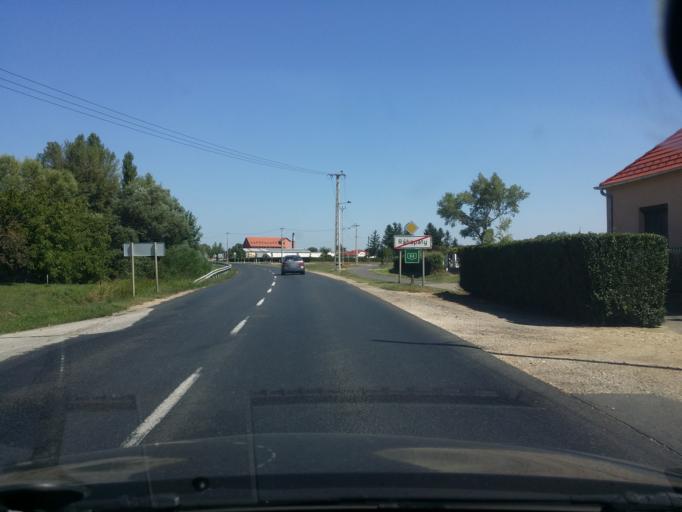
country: HU
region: Vas
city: Sarvar
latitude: 47.3069
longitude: 16.9282
